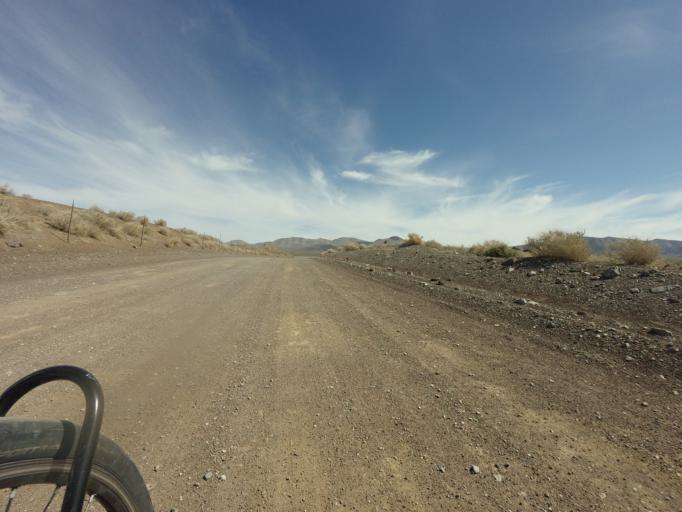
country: US
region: California
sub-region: Kern County
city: Inyokern
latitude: 35.9773
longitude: -117.9171
